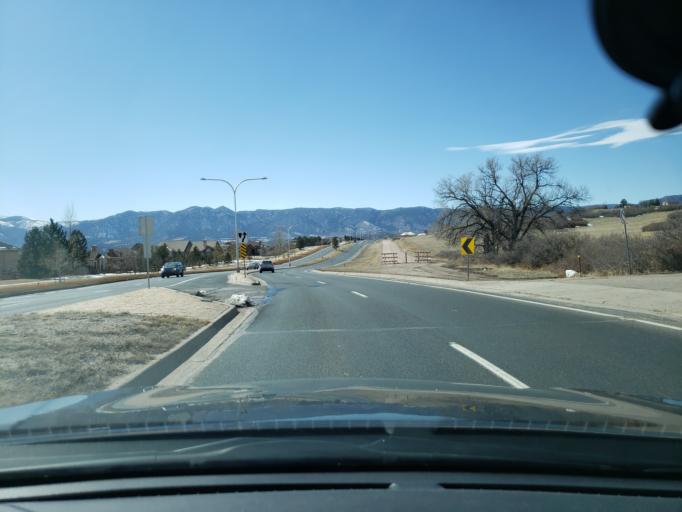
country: US
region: Colorado
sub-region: El Paso County
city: Gleneagle
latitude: 39.0274
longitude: -104.8018
